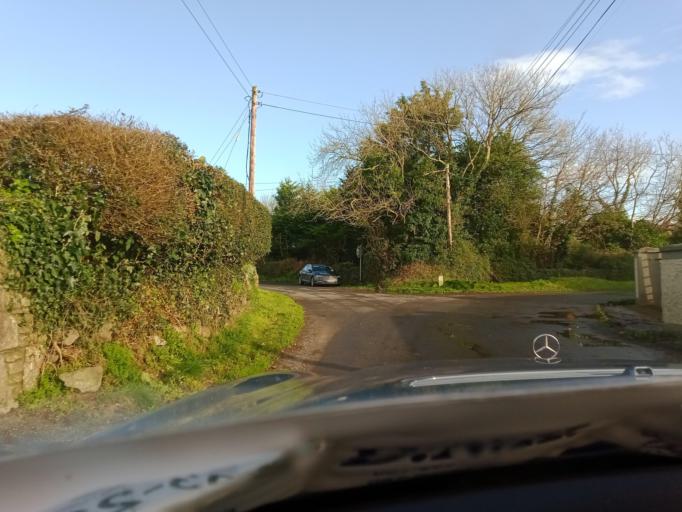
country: IE
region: Leinster
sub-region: Kilkenny
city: Mooncoin
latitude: 52.2818
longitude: -7.2588
